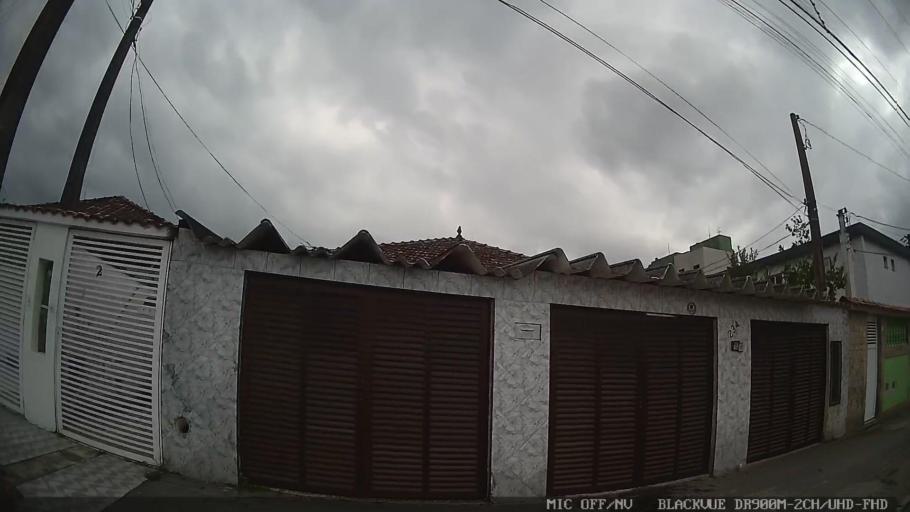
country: BR
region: Sao Paulo
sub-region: Guaruja
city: Guaruja
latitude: -23.9920
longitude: -46.2892
